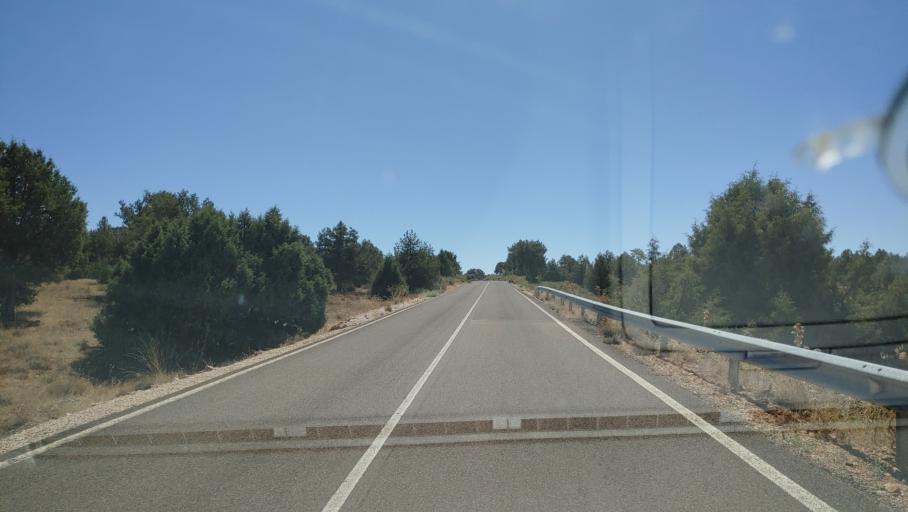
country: ES
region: Castille-La Mancha
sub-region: Provincia de Albacete
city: Ossa de Montiel
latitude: 38.8640
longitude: -2.8003
